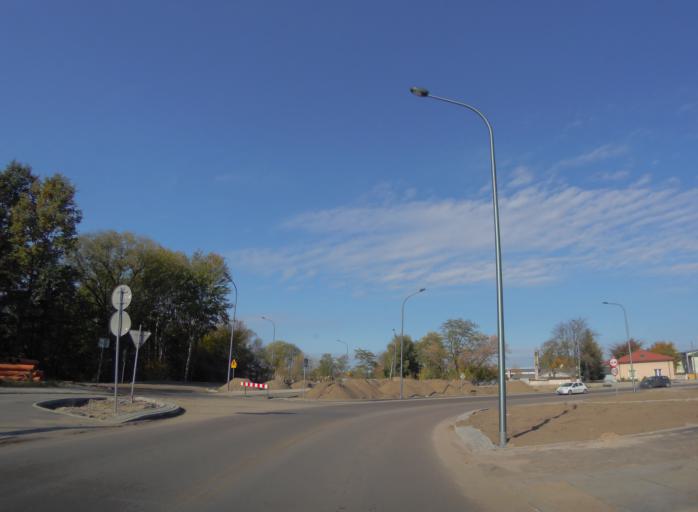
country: PL
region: Masovian Voivodeship
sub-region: Warszawa
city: Wawer
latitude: 52.1667
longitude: 21.1580
